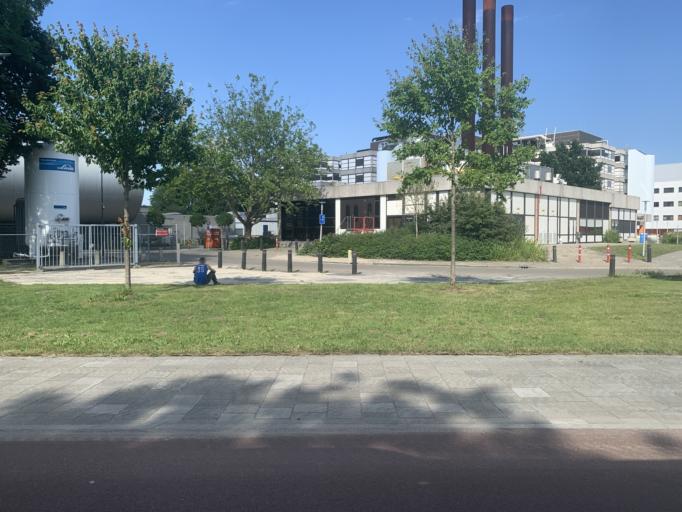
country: NL
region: Groningen
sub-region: Gemeente Groningen
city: Groningen
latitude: 53.1912
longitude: 6.5486
